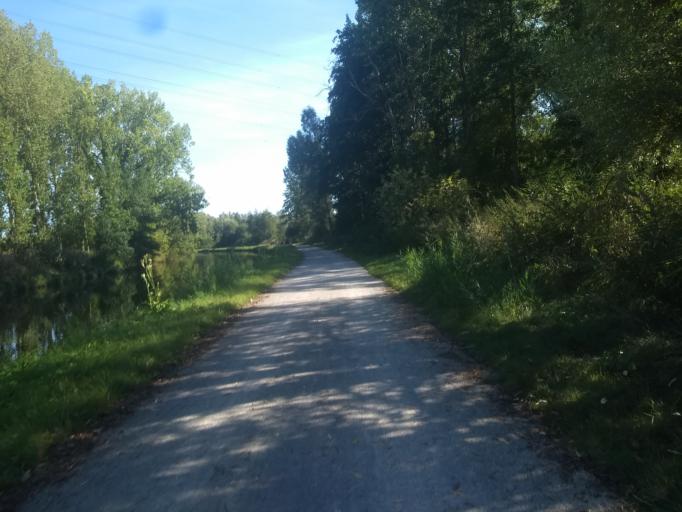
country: FR
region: Nord-Pas-de-Calais
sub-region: Departement du Pas-de-Calais
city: Fampoux
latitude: 50.2971
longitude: 2.8796
